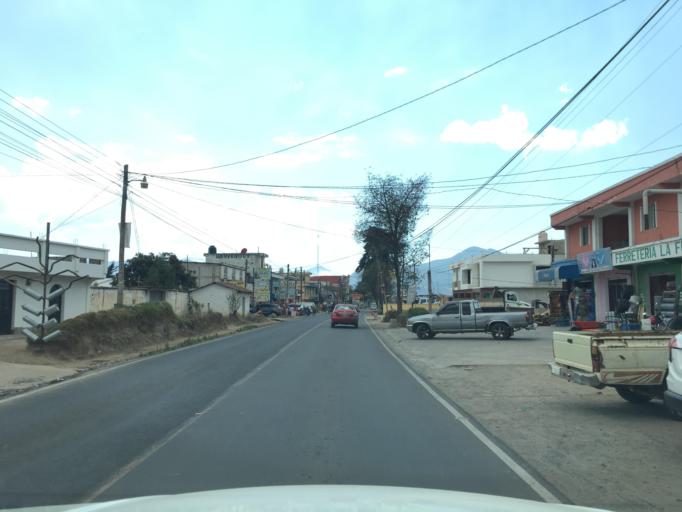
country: GT
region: Quetzaltenango
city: Olintepeque
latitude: 14.8765
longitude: -91.5138
